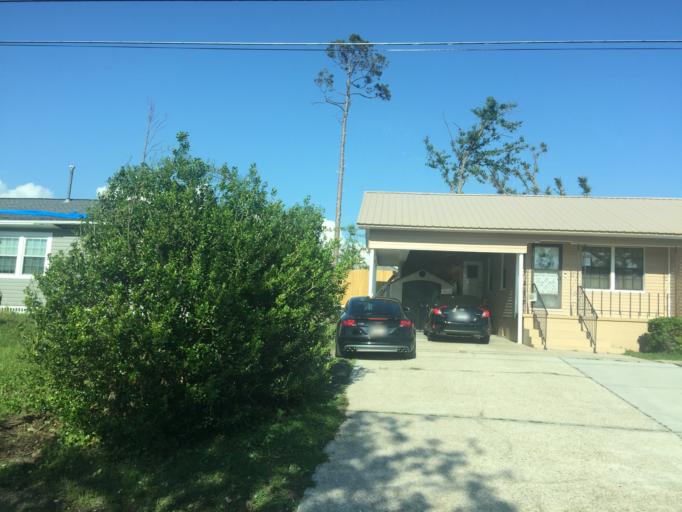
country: US
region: Florida
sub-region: Bay County
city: Panama City
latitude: 30.1503
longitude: -85.6492
